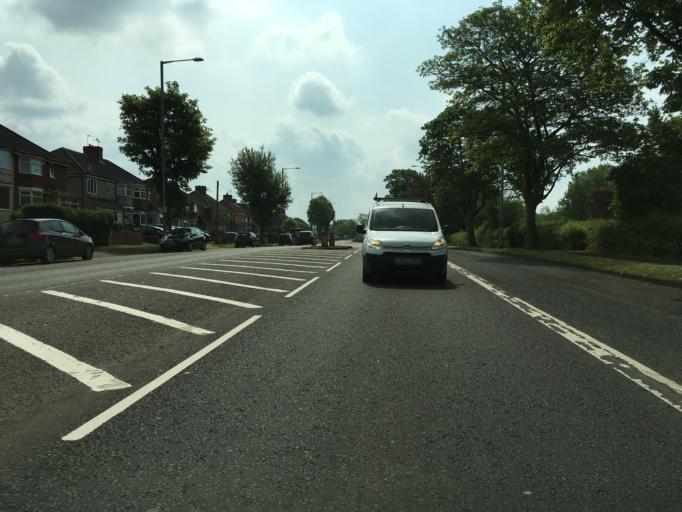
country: GB
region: England
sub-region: North Somerset
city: Easton-in-Gordano
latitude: 51.4869
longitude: -2.6840
